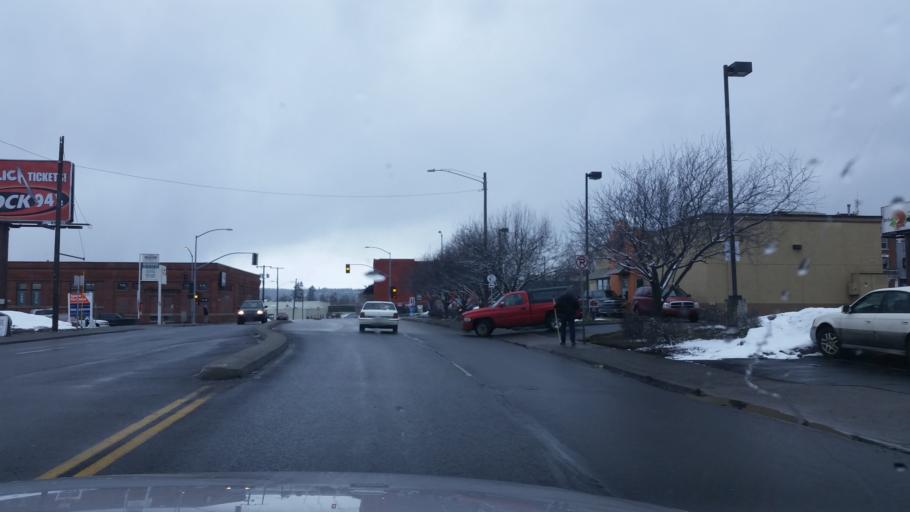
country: US
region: Washington
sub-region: Spokane County
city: Spokane
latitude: 47.6681
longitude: -117.4254
